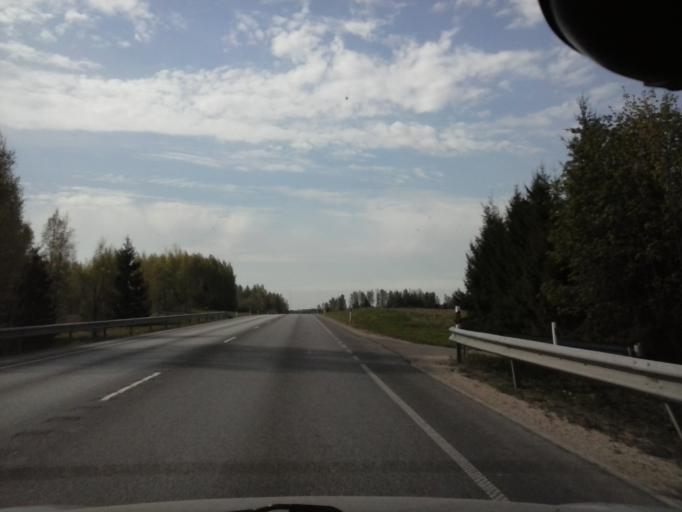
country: EE
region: Tartu
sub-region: UElenurme vald
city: Ulenurme
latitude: 58.1850
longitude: 26.6932
